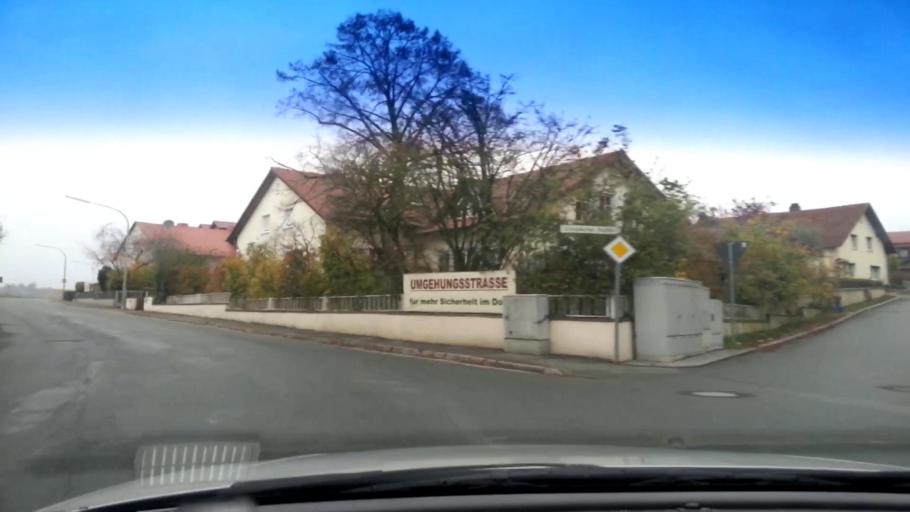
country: DE
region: Bavaria
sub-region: Upper Franconia
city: Litzendorf
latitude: 49.8827
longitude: 11.0140
